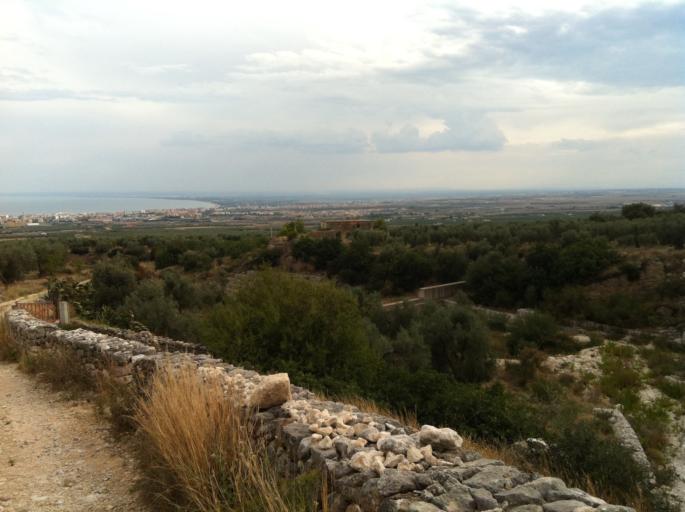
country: IT
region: Apulia
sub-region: Provincia di Foggia
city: Manfredonia
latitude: 41.6659
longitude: 15.9116
